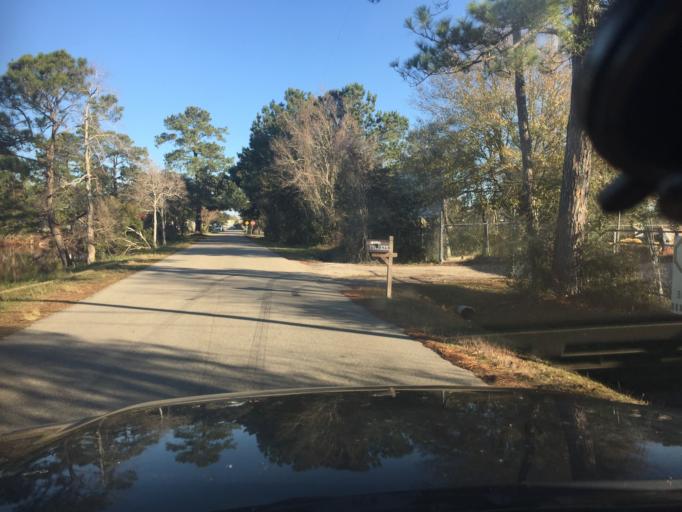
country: US
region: Louisiana
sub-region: Saint Tammany Parish
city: Slidell
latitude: 30.2519
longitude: -89.7635
